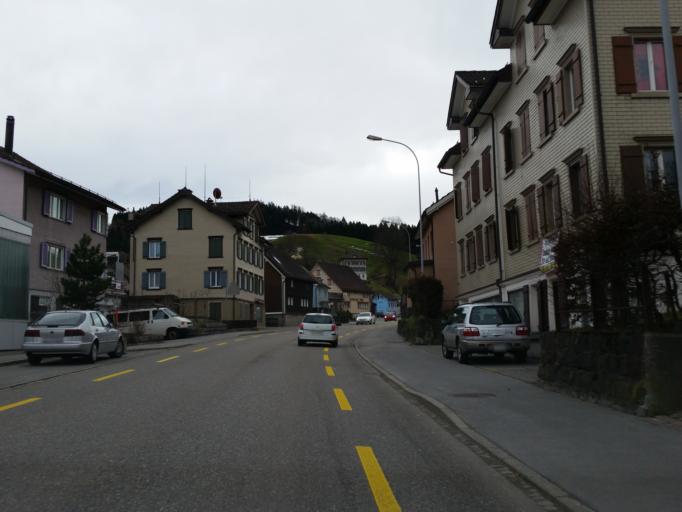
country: CH
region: Appenzell Ausserrhoden
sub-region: Bezirk Hinterland
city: Herisau
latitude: 47.3751
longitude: 9.2805
